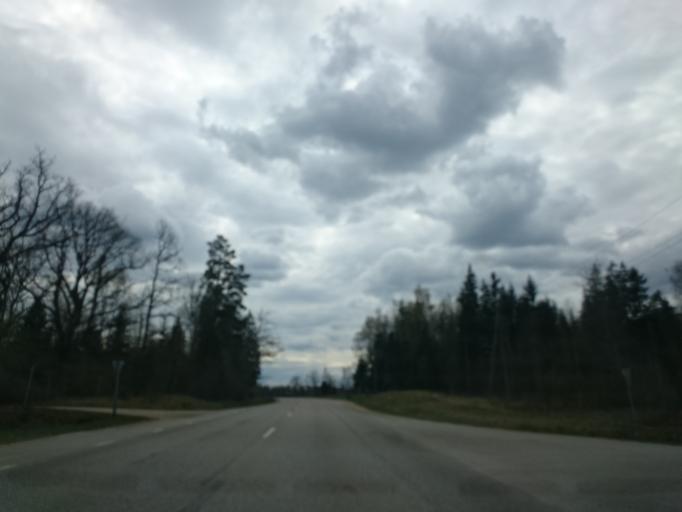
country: LV
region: Kuldigas Rajons
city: Kuldiga
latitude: 56.8865
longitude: 21.8804
